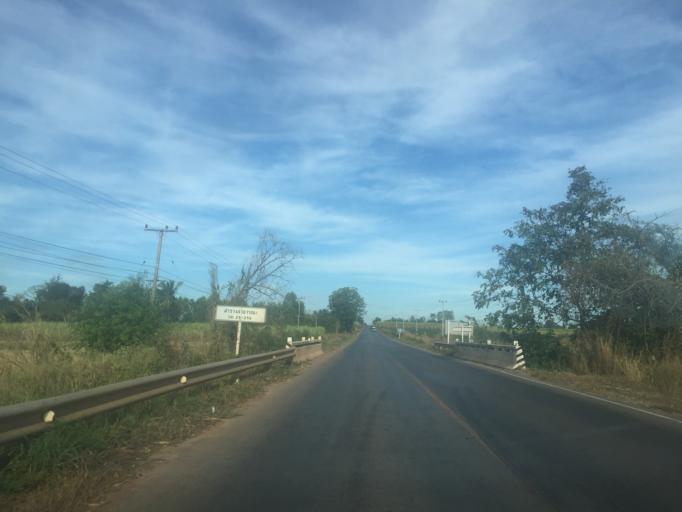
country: TH
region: Changwat Udon Thani
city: Si That
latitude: 16.9897
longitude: 103.1533
